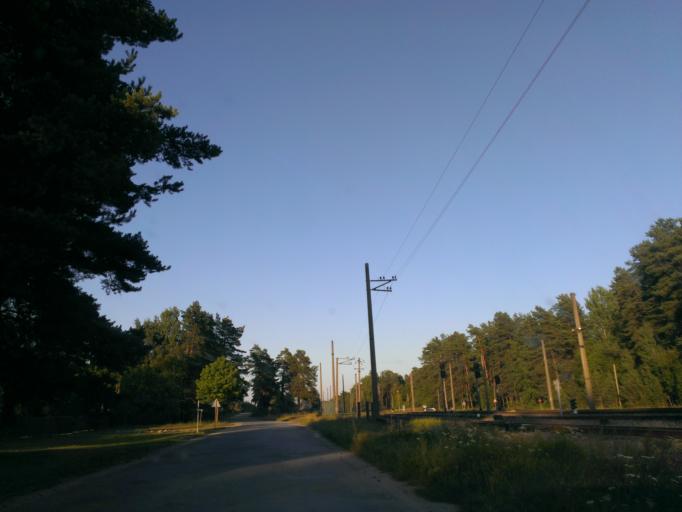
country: LV
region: Garkalne
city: Garkalne
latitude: 57.0490
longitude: 24.4207
